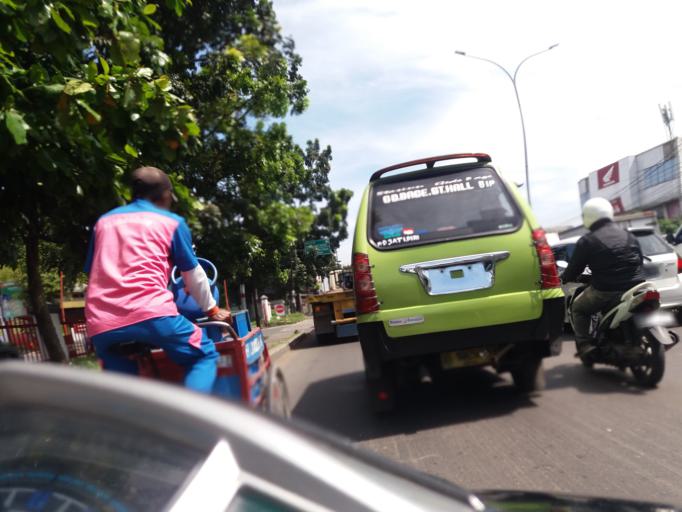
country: ID
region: West Java
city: Bandung
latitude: -6.9475
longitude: 107.6354
